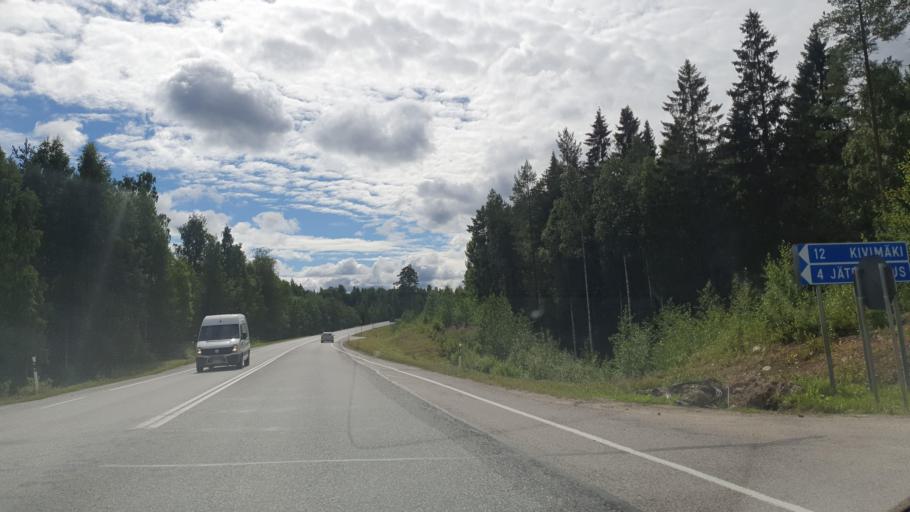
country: FI
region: Kainuu
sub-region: Kajaani
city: Kajaani
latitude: 64.1854
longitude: 27.5975
